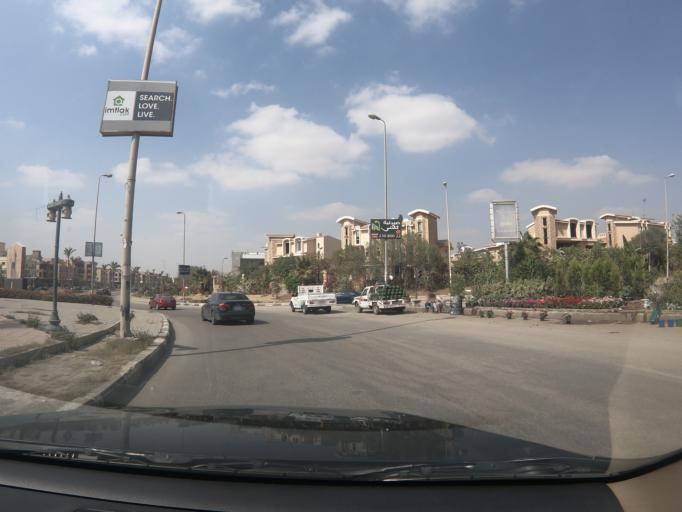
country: EG
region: Muhafazat al Qalyubiyah
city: Al Khankah
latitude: 30.0365
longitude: 31.4754
